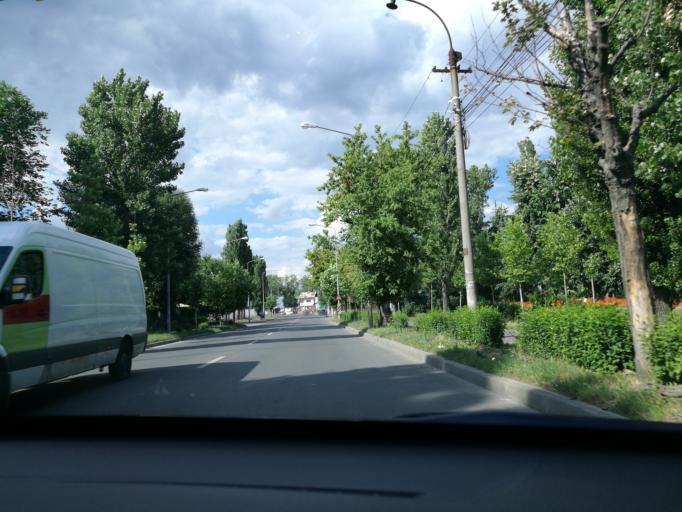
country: RO
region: Ilfov
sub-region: Comuna Glina
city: Catelu
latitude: 44.4244
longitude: 26.2202
